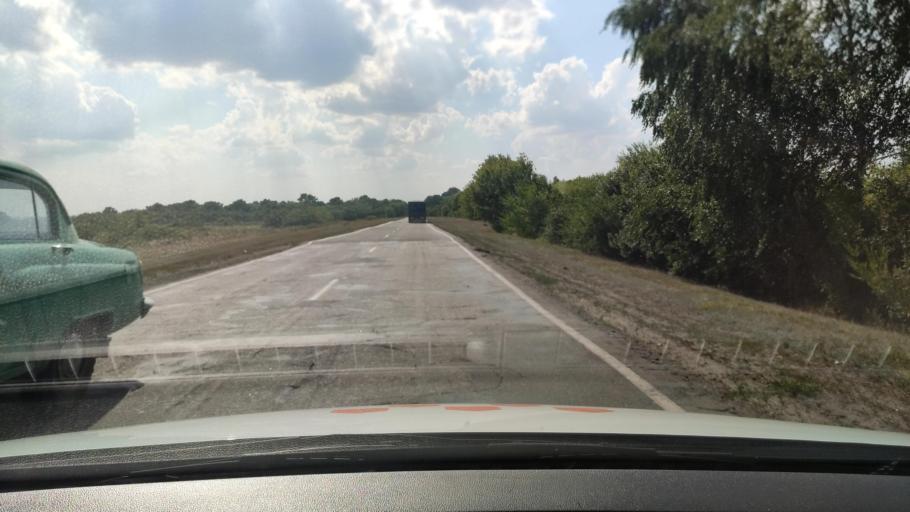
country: RU
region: Voronezj
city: Sadovoye
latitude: 51.7764
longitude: 40.5220
